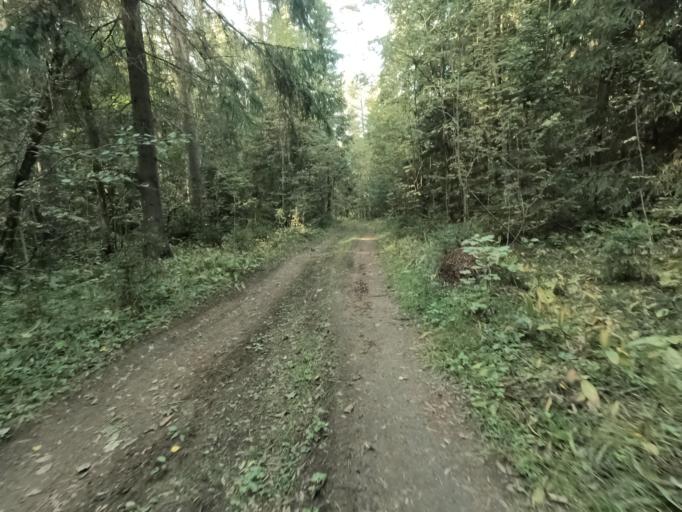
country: RU
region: Leningrad
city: Imeni Sverdlova
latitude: 59.8417
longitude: 30.7295
